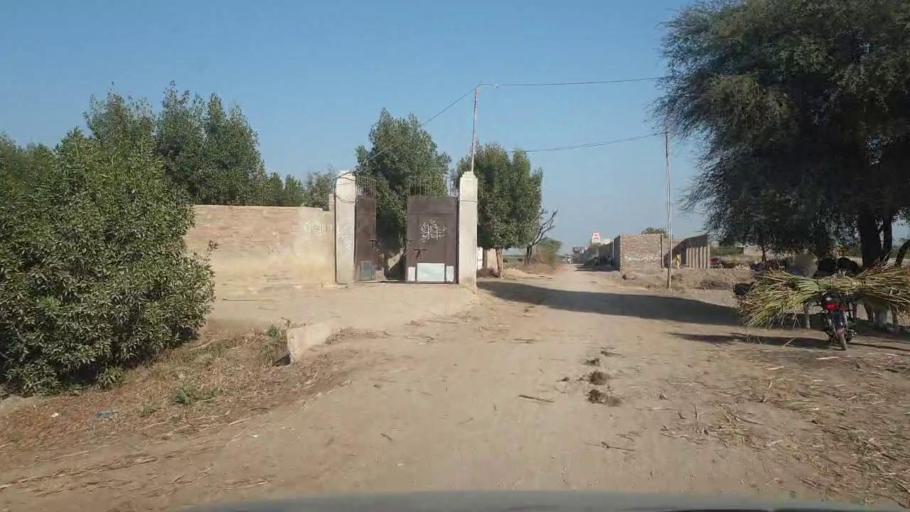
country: PK
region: Sindh
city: Chambar
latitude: 25.2882
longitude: 68.8660
